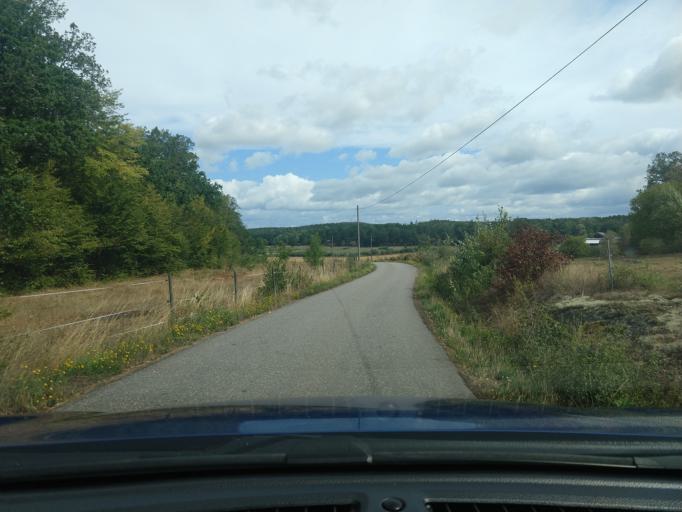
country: SE
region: Blekinge
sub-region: Ronneby Kommun
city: Brakne-Hoby
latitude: 56.2938
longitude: 15.1963
